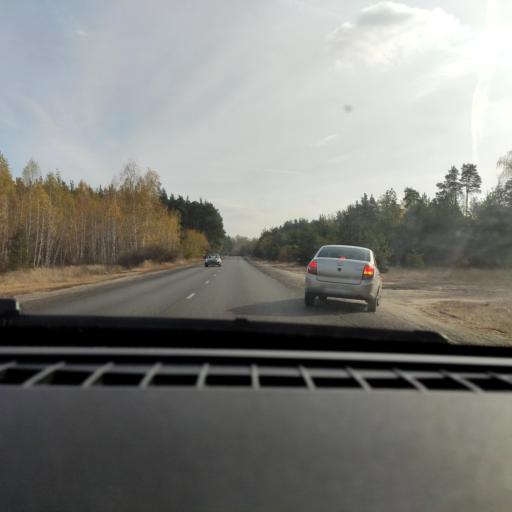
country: RU
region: Voronezj
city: Maslovka
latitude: 51.5790
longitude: 39.2895
